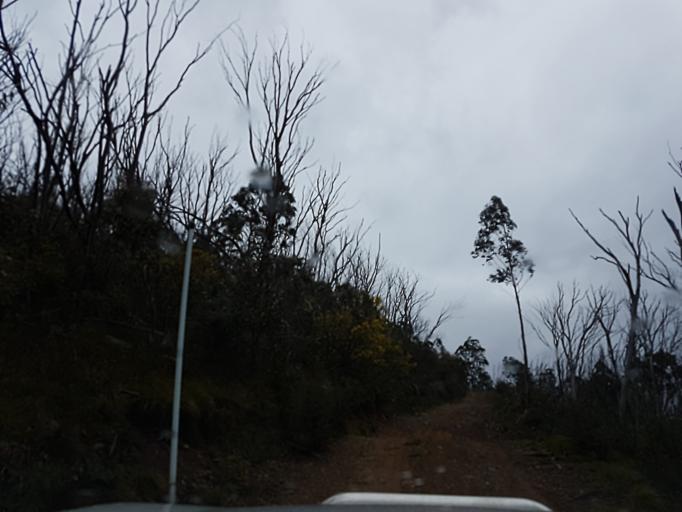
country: AU
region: Victoria
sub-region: Alpine
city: Mount Beauty
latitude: -37.0919
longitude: 147.0942
